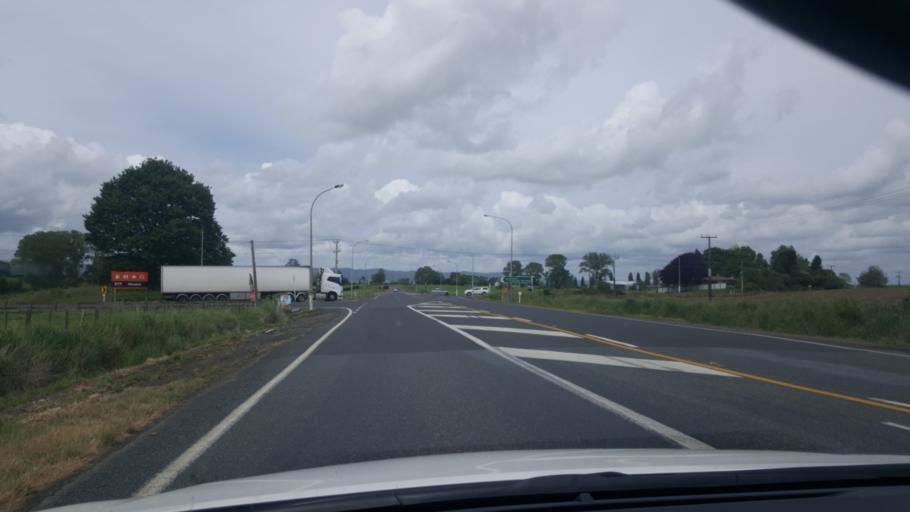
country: NZ
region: Waikato
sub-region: Matamata-Piako District
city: Matamata
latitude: -37.8880
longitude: 175.7742
